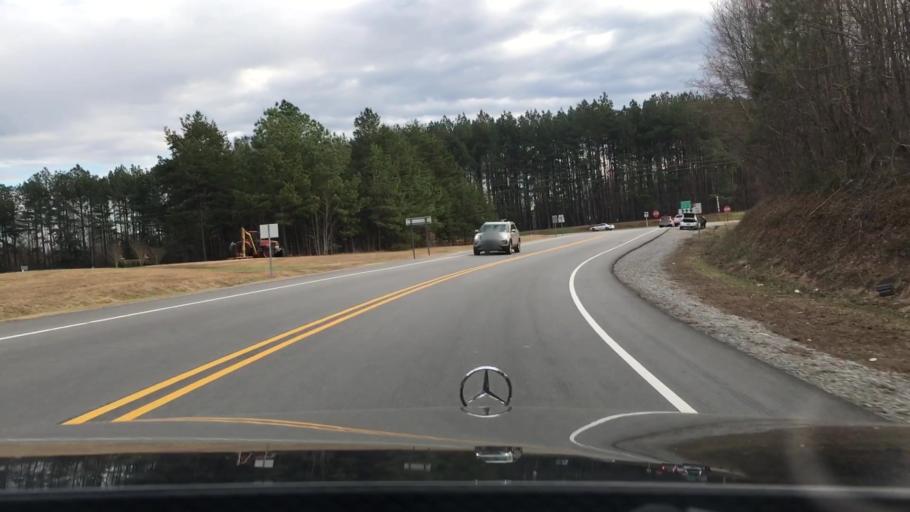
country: US
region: North Carolina
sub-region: Caswell County
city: Yanceyville
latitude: 36.4069
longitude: -79.3223
